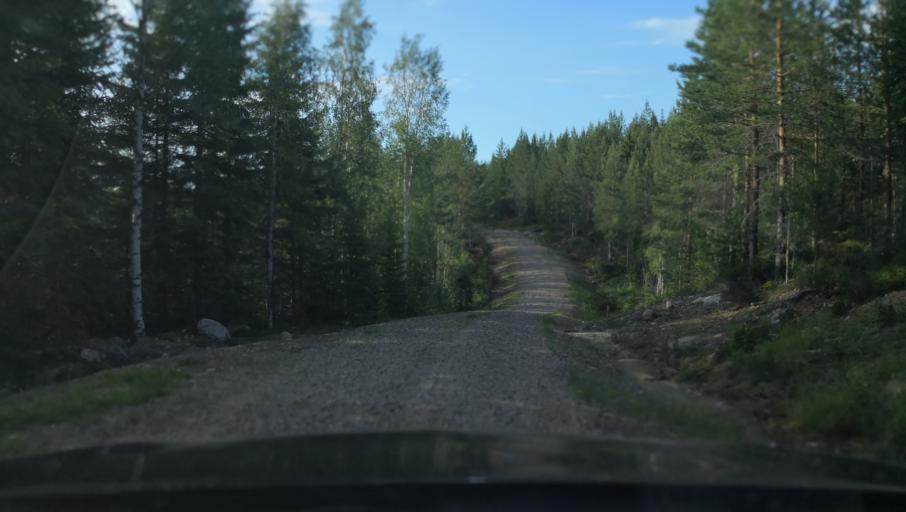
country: SE
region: Dalarna
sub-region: Smedjebackens Kommun
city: Smedjebacken
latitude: 60.0642
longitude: 15.3085
